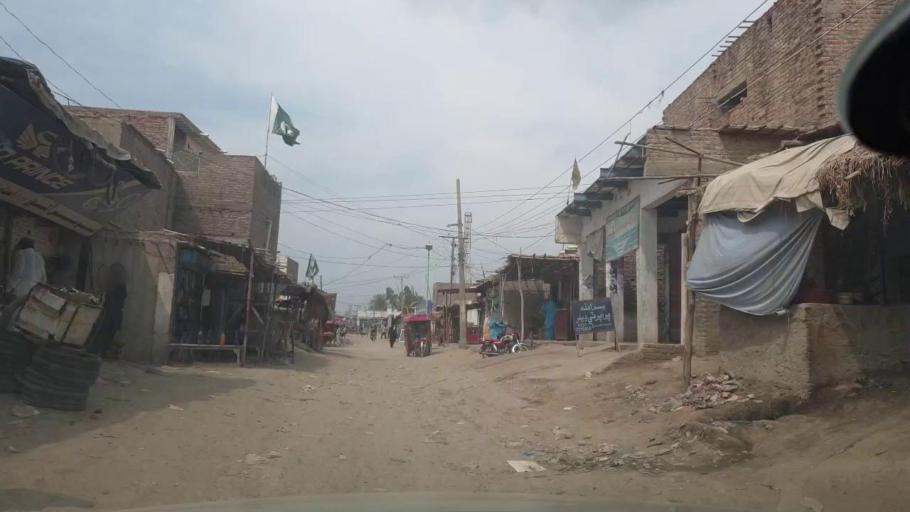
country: PK
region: Sindh
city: Jacobabad
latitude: 28.2676
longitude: 68.4378
